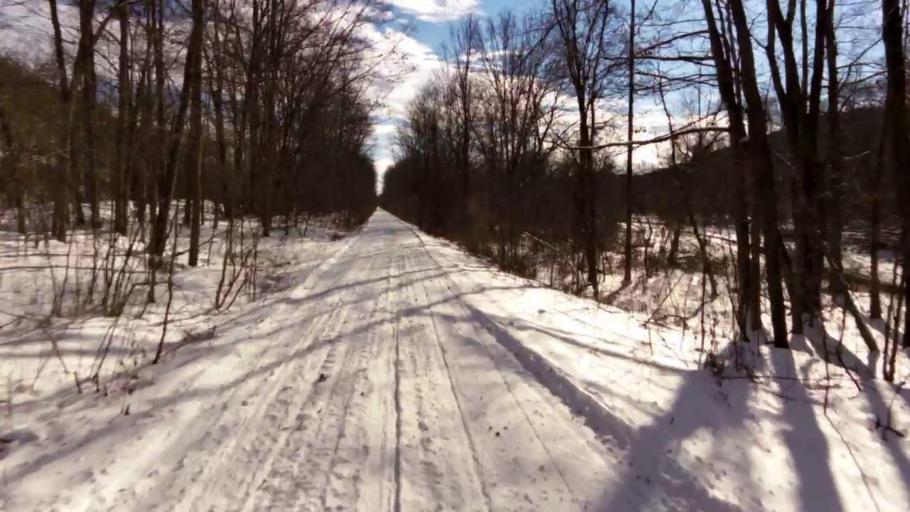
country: US
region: Pennsylvania
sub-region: McKean County
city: Foster Brook
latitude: 42.0577
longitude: -78.6375
